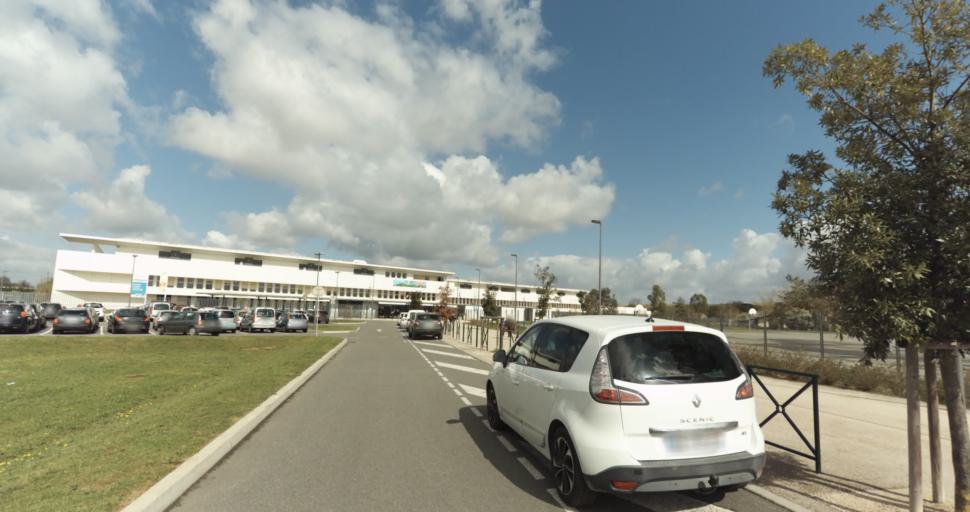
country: FR
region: Midi-Pyrenees
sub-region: Departement de la Haute-Garonne
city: Auterive
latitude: 43.3558
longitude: 1.4646
